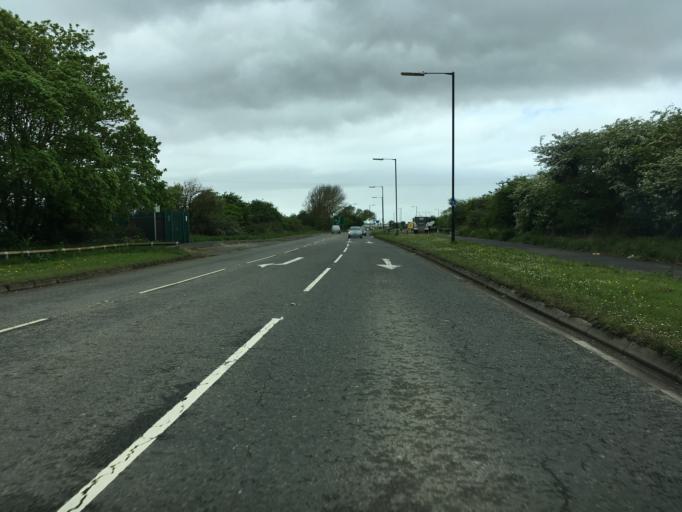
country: GB
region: England
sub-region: North Somerset
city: Hutton
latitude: 51.3384
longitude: -2.9240
